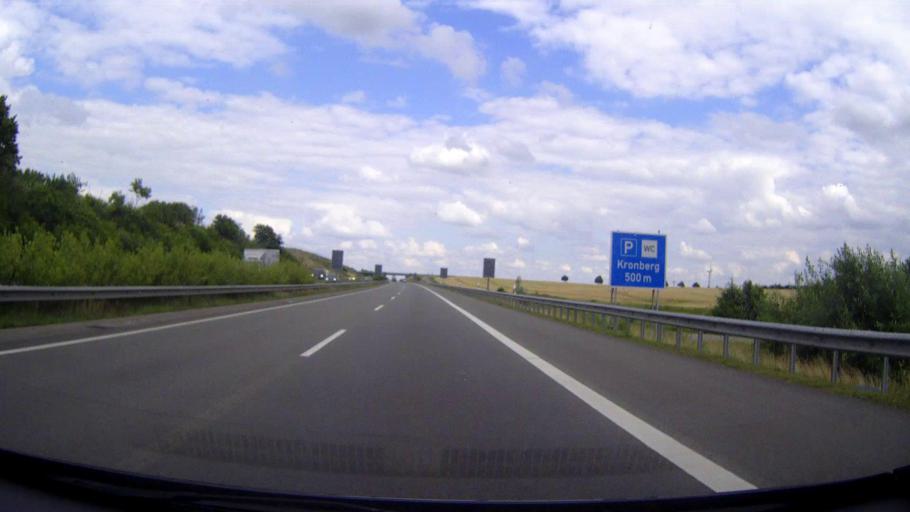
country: DE
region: Schleswig-Holstein
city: Weede
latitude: 53.9184
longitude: 10.3731
